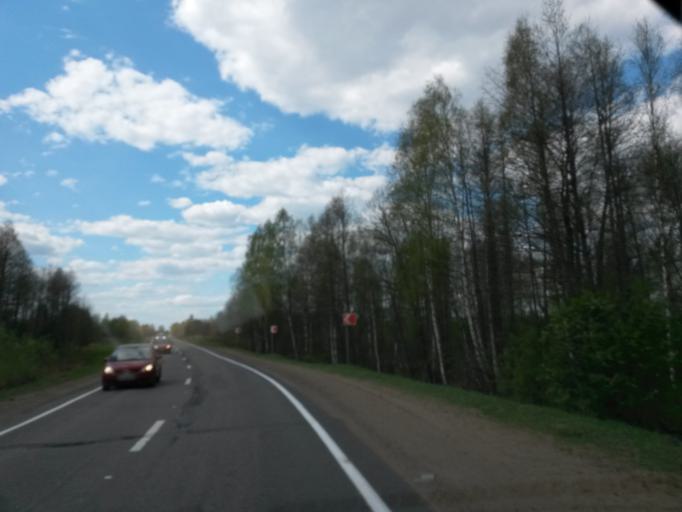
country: RU
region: Jaroslavl
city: Bol'shoye Selo
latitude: 57.6889
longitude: 39.2286
